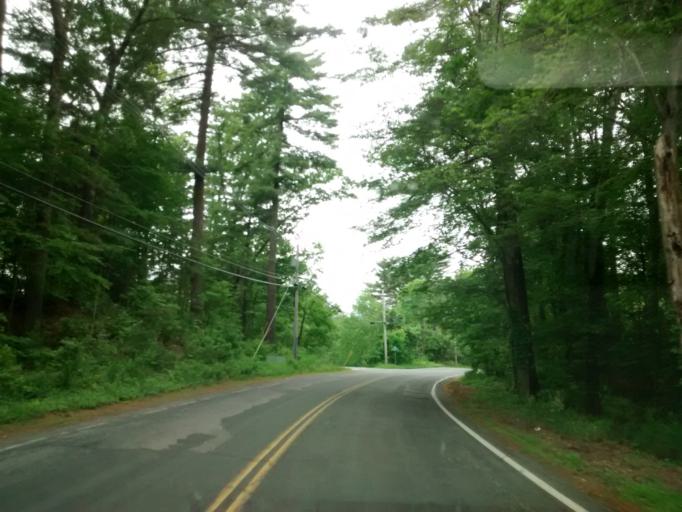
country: US
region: Massachusetts
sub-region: Worcester County
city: Whitinsville
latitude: 42.1039
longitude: -71.6864
